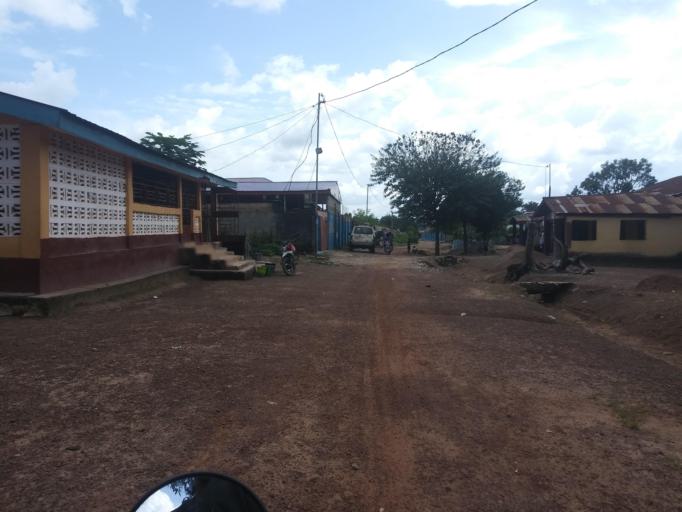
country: SL
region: Northern Province
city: Makeni
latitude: 8.8734
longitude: -12.0424
